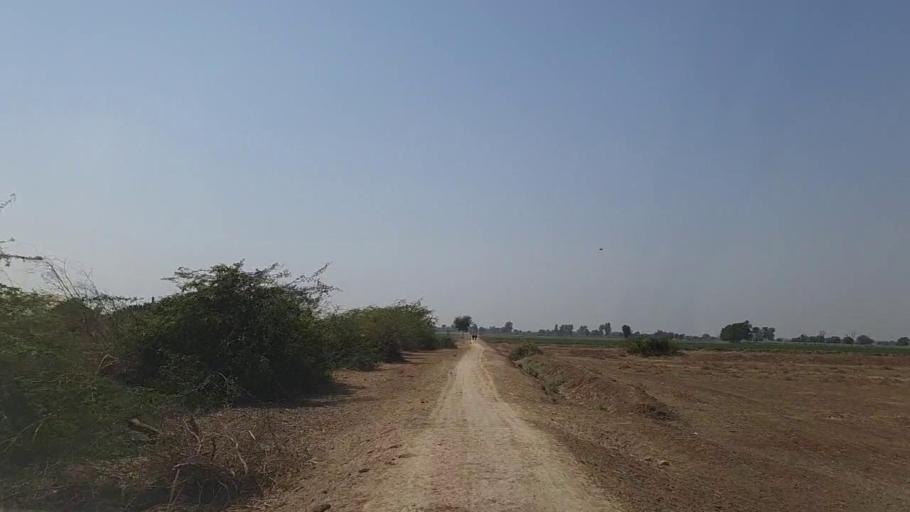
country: PK
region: Sindh
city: Samaro
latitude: 25.2541
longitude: 69.3909
